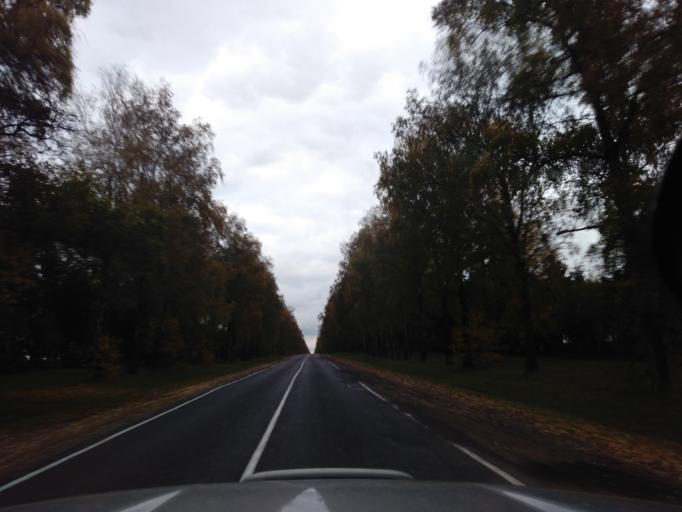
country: BY
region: Minsk
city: Slutsk
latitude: 53.2173
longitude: 27.4234
